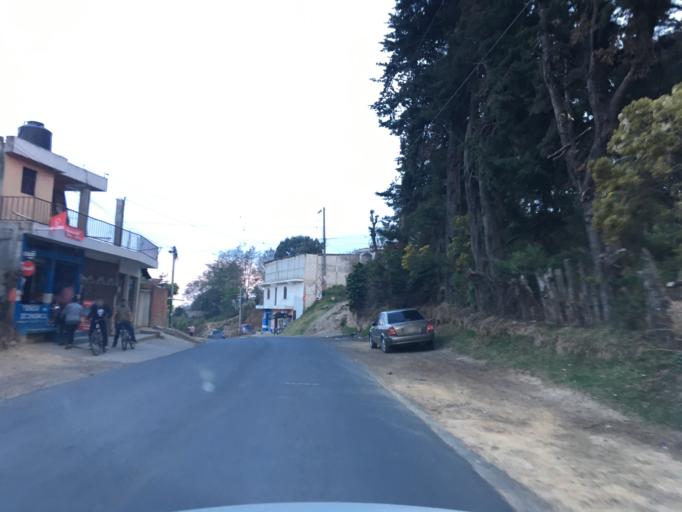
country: GT
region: Chimaltenango
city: Tecpan Guatemala
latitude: 14.7504
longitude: -91.0008
